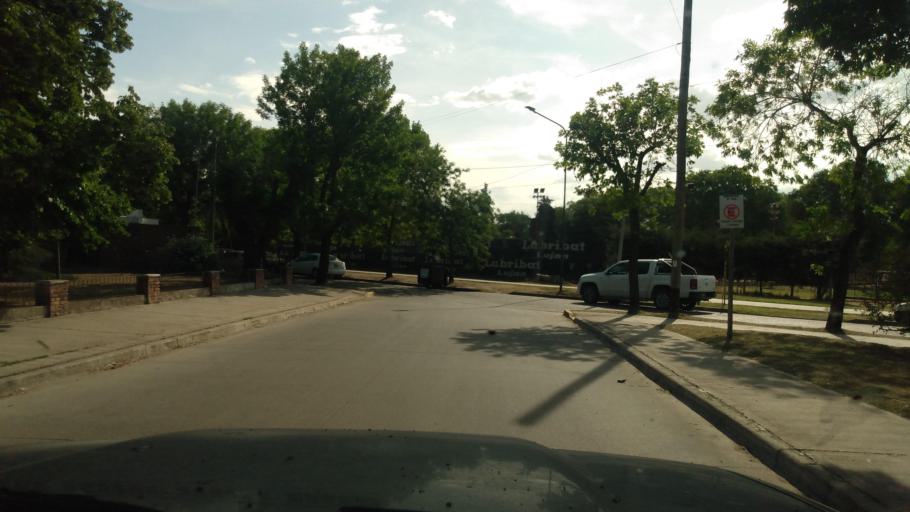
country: AR
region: Buenos Aires
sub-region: Partido de Lujan
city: Lujan
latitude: -34.5603
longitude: -59.1105
